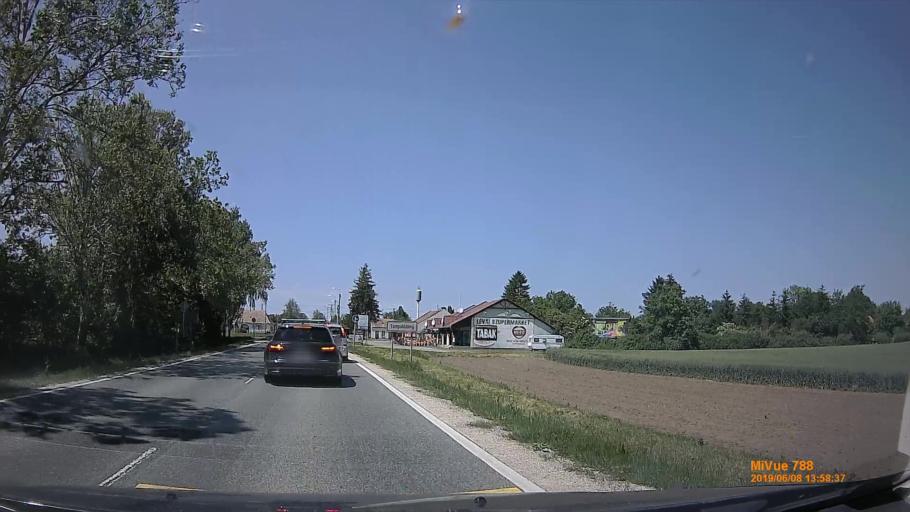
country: HU
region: Vas
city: Buk
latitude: 47.3781
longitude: 16.8826
